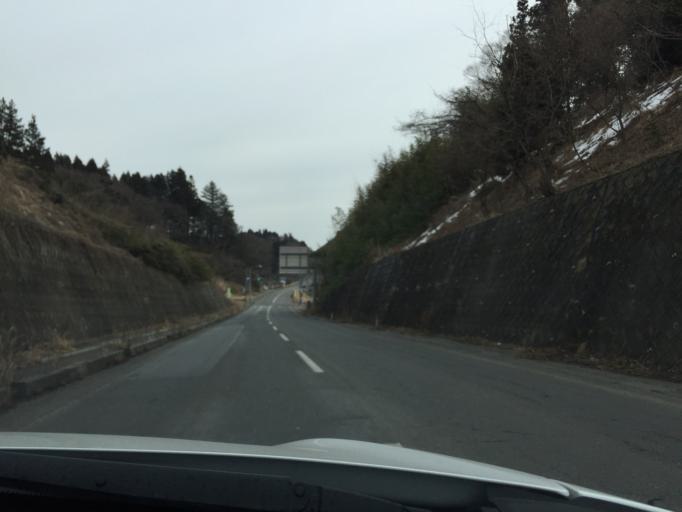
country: JP
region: Fukushima
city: Funehikimachi-funehiki
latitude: 37.2816
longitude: 140.6209
